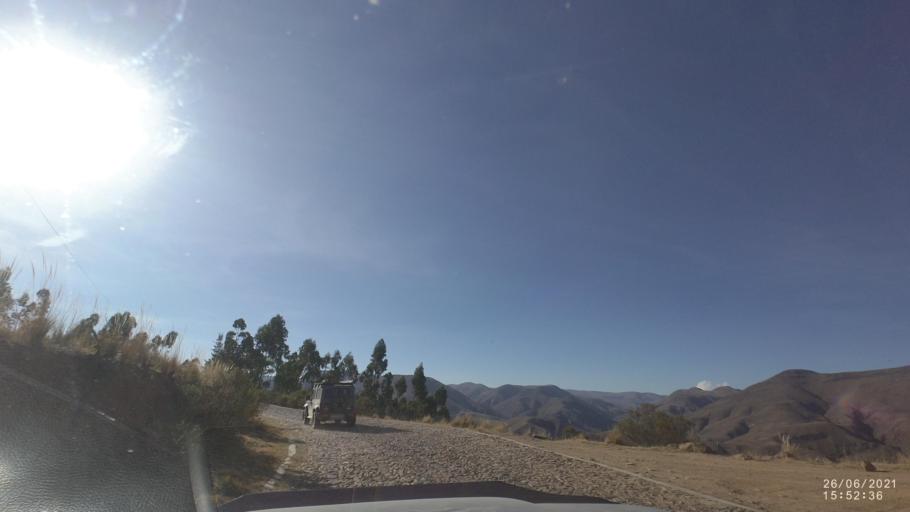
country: BO
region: Cochabamba
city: Arani
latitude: -17.8378
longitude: -65.7025
